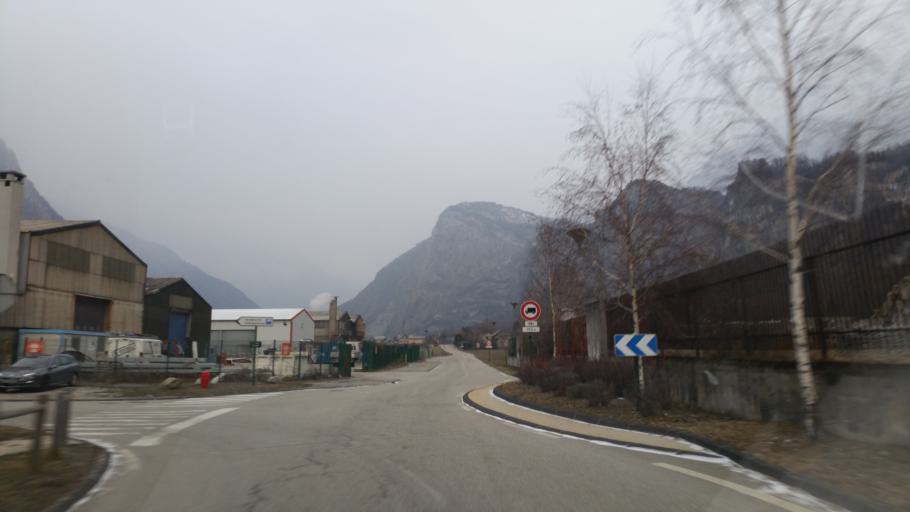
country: FR
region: Rhone-Alpes
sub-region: Departement de la Savoie
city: Saint-Jean-de-Maurienne
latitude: 45.3052
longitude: 6.3509
